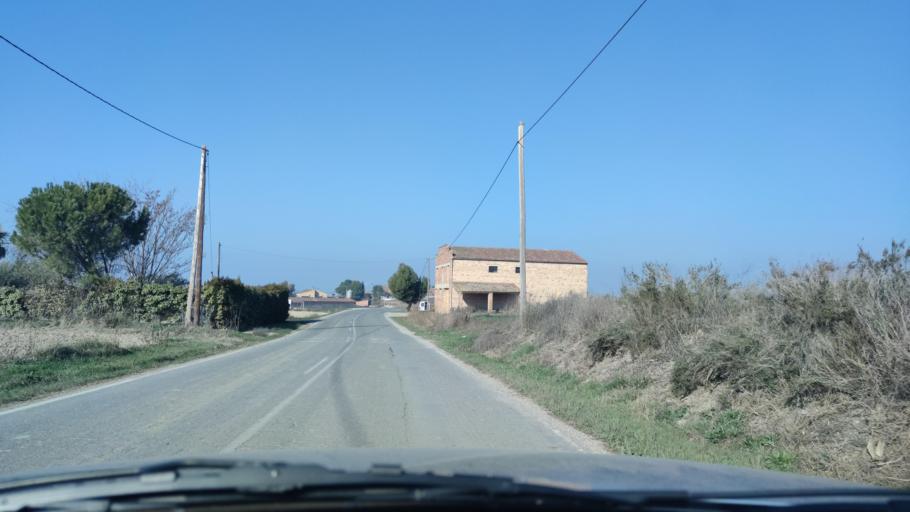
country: ES
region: Catalonia
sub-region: Provincia de Lleida
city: Alcoletge
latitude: 41.6175
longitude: 0.7350
